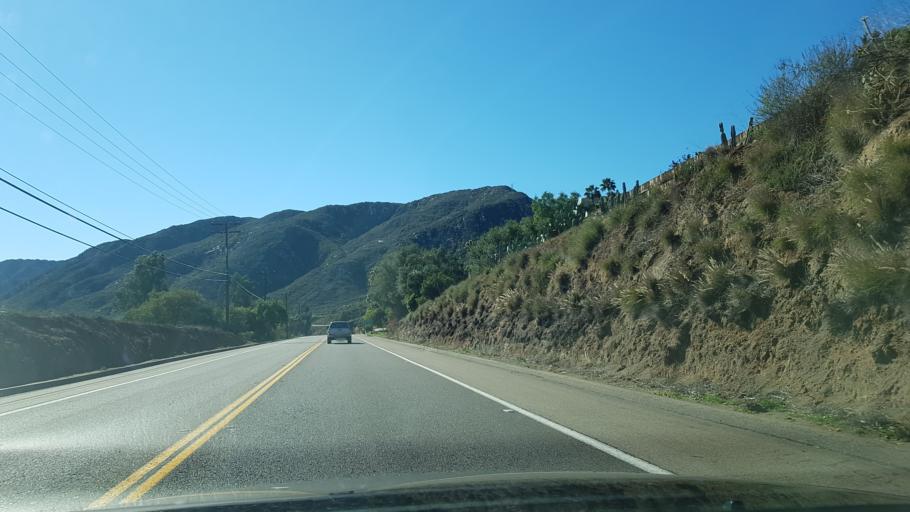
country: US
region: California
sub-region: San Diego County
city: Escondido
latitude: 33.0864
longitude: -117.1162
